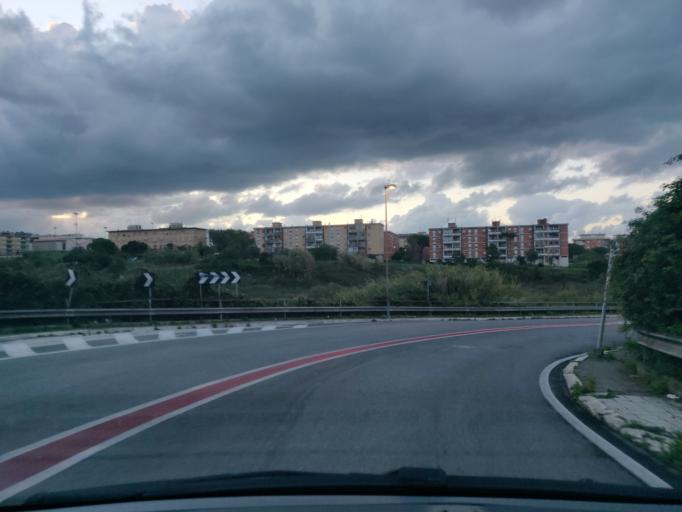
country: IT
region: Latium
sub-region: Citta metropolitana di Roma Capitale
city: Civitavecchia
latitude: 42.0850
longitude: 11.8087
